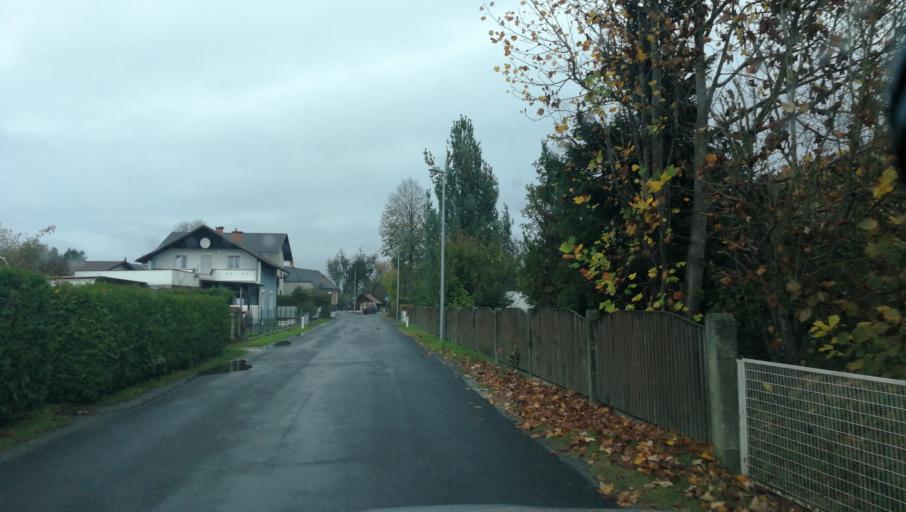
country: AT
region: Styria
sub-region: Politischer Bezirk Leibnitz
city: Strass in Steiermark
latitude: 46.7244
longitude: 15.6300
